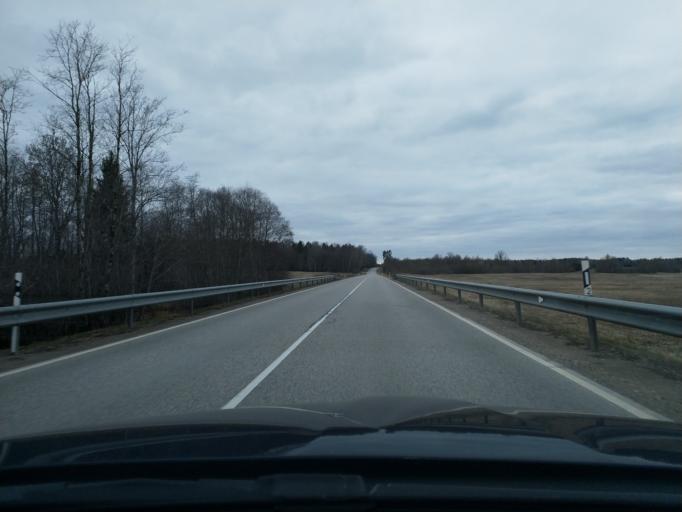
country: LV
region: Kuldigas Rajons
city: Kuldiga
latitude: 56.9666
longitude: 22.0583
